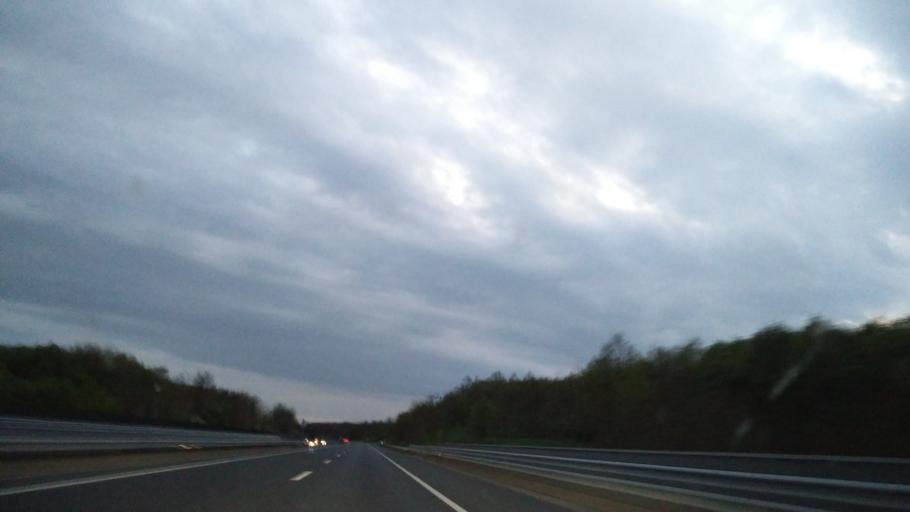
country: HU
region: Somogy
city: Balatonfoldvar
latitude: 46.8180
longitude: 17.8944
